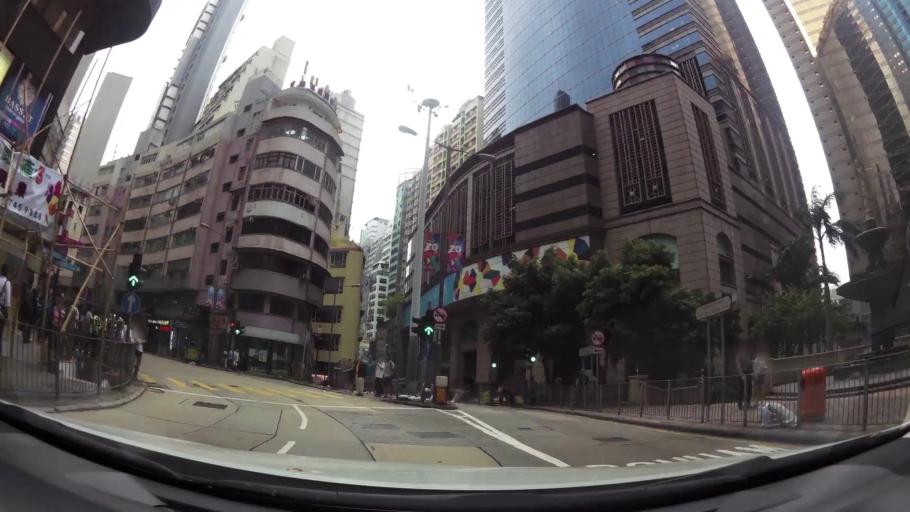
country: HK
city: Hong Kong
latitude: 22.2849
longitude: 114.1530
